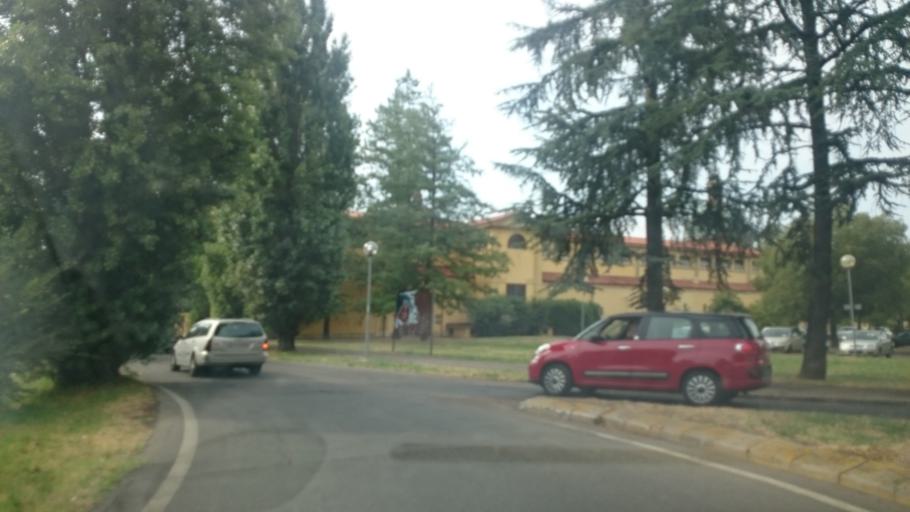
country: IT
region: Emilia-Romagna
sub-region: Provincia di Reggio Emilia
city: Reggio nell'Emilia
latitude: 44.6907
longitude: 10.6238
